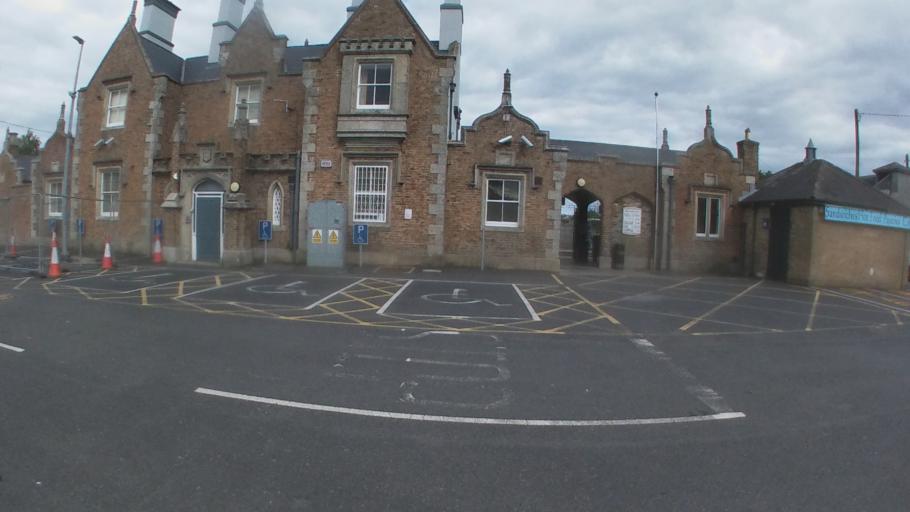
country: IE
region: Leinster
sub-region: County Carlow
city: Carlow
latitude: 52.8408
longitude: -6.9229
